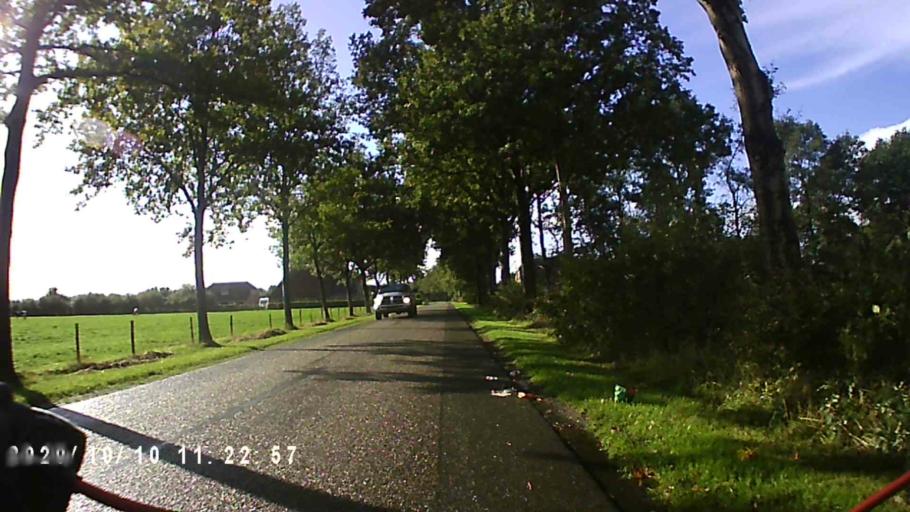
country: NL
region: Friesland
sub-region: Gemeente Smallingerland
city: Drachtstercompagnie
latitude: 53.0916
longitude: 6.1775
